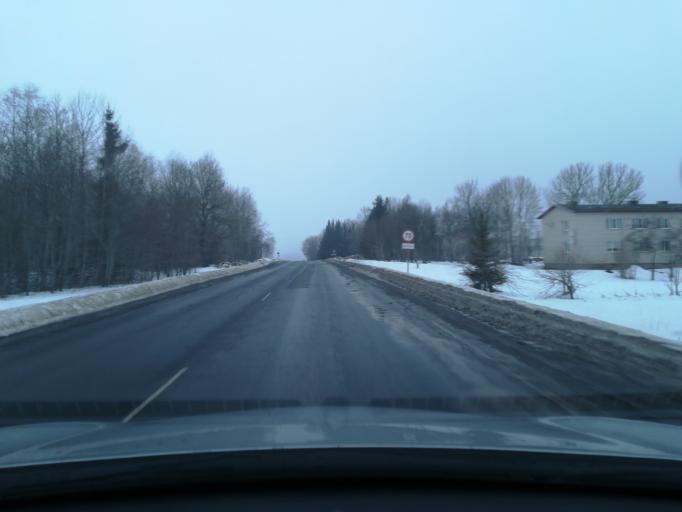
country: EE
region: Harju
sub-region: Raasiku vald
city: Arukula
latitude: 59.3466
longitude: 25.1013
